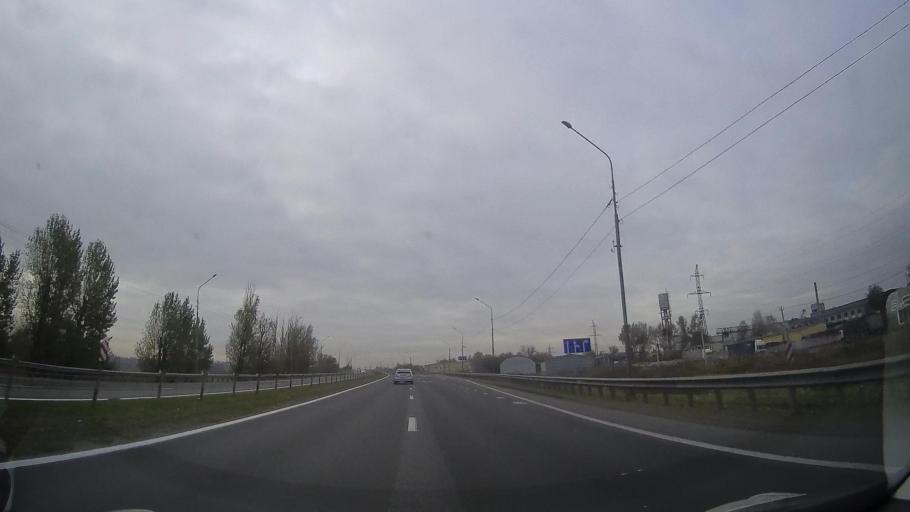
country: RU
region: Rostov
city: Bataysk
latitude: 47.1093
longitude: 39.7653
